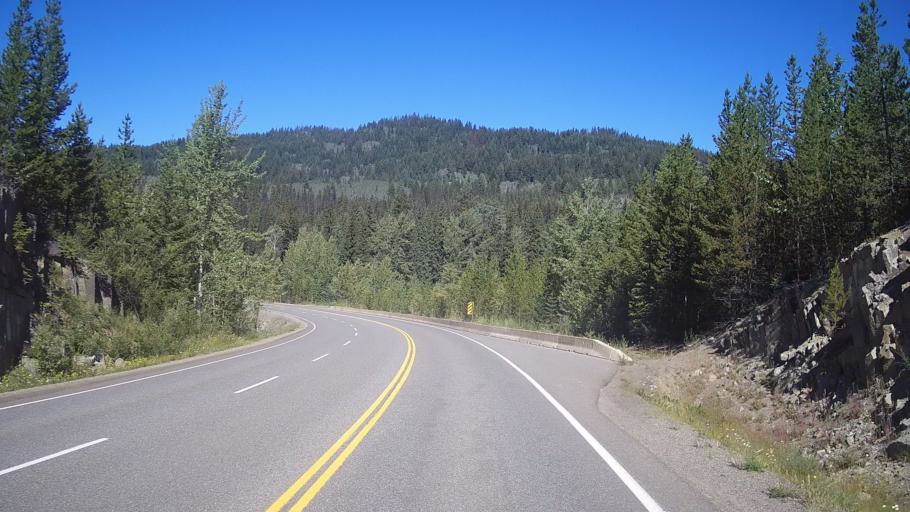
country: CA
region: British Columbia
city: Kamloops
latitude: 51.4772
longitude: -120.4832
